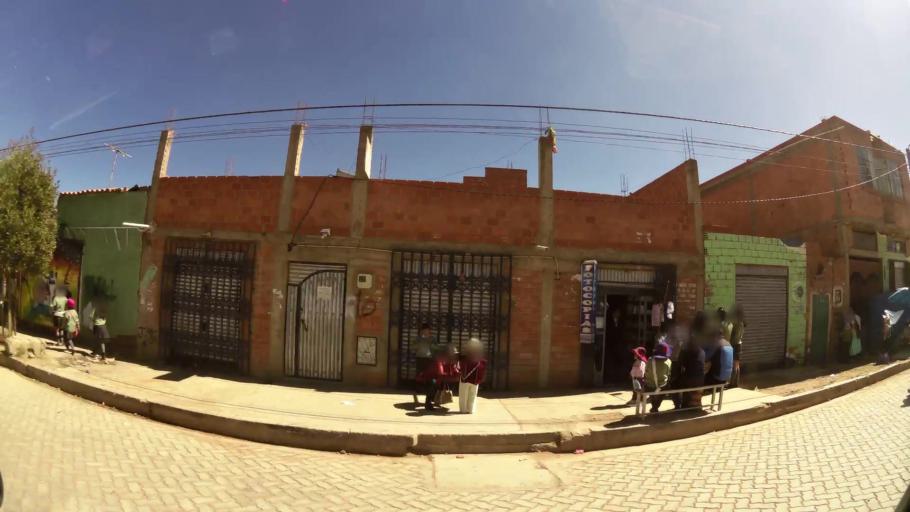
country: BO
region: La Paz
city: La Paz
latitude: -16.5371
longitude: -68.1943
